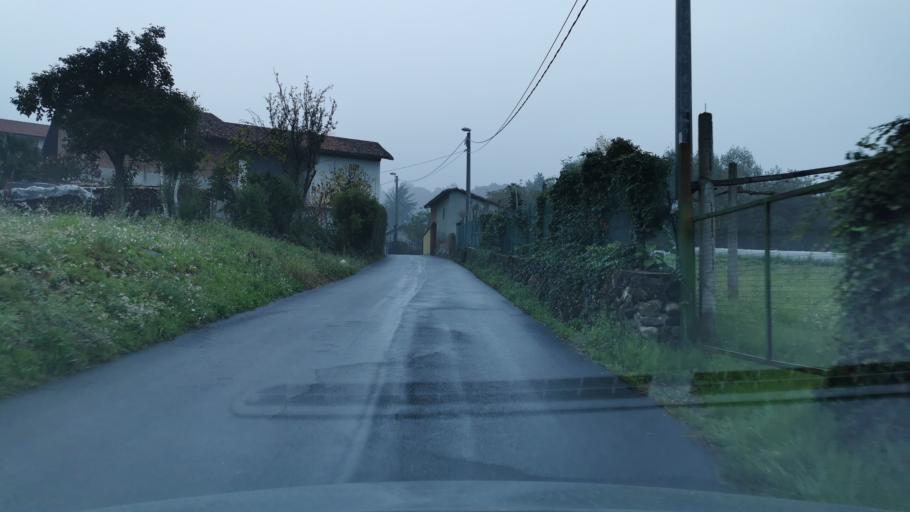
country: IT
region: Piedmont
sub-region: Provincia di Torino
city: Aglie
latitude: 45.3687
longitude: 7.7922
